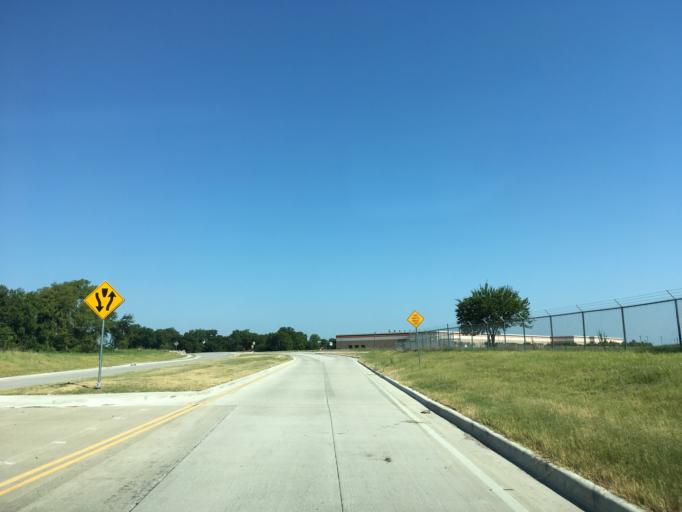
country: US
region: Texas
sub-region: Collin County
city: Fairview
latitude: 33.1641
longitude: -96.5948
